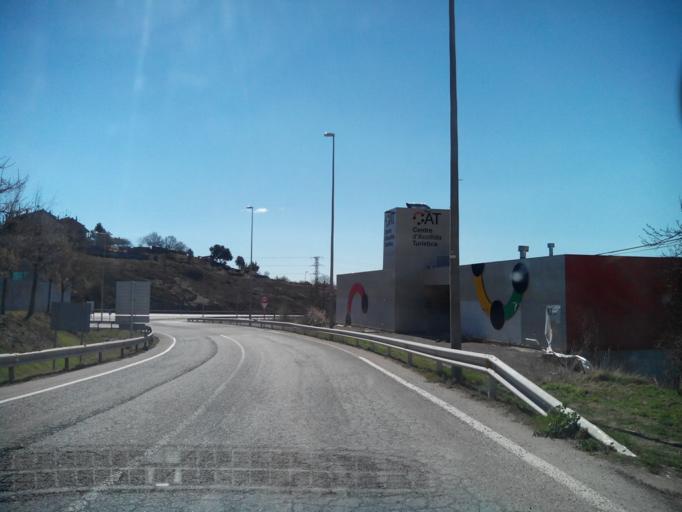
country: ES
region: Catalonia
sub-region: Provincia de Barcelona
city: Berga
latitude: 42.1024
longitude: 1.8571
